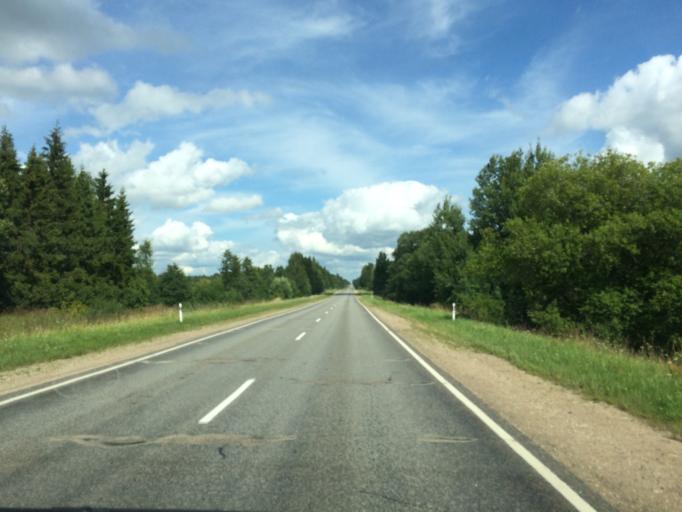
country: LV
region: Rezekne
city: Rezekne
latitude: 56.6385
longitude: 27.4779
